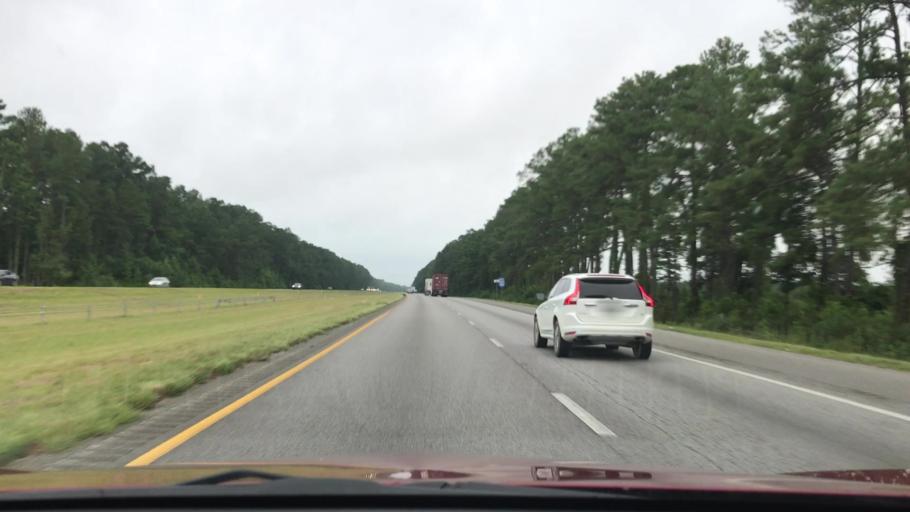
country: US
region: South Carolina
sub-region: Dorchester County
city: Summerville
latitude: 33.0846
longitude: -80.2114
